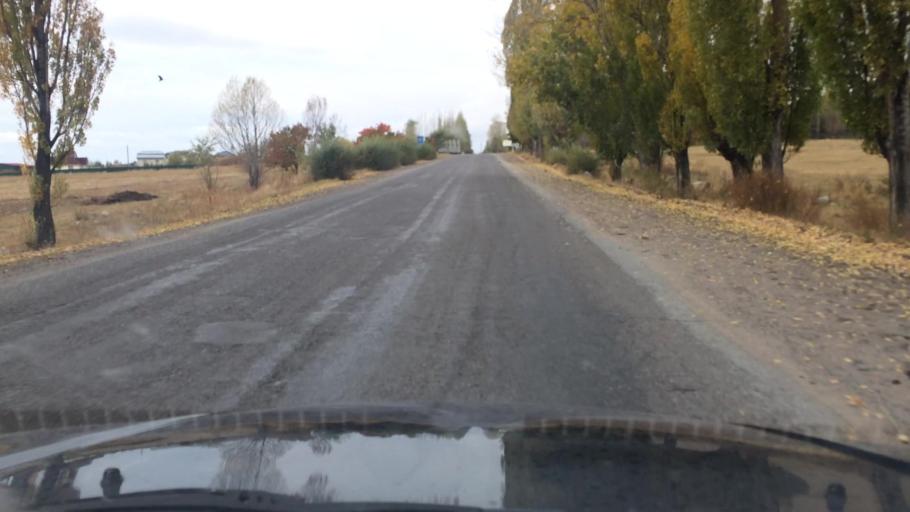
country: KG
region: Ysyk-Koel
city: Pokrovka
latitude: 42.7367
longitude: 77.9518
